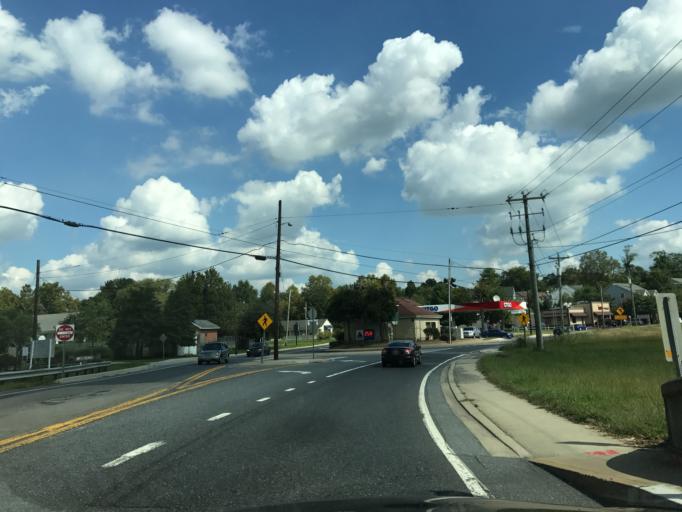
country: US
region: Maryland
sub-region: Queen Anne's County
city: Centreville
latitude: 39.0401
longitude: -76.0724
